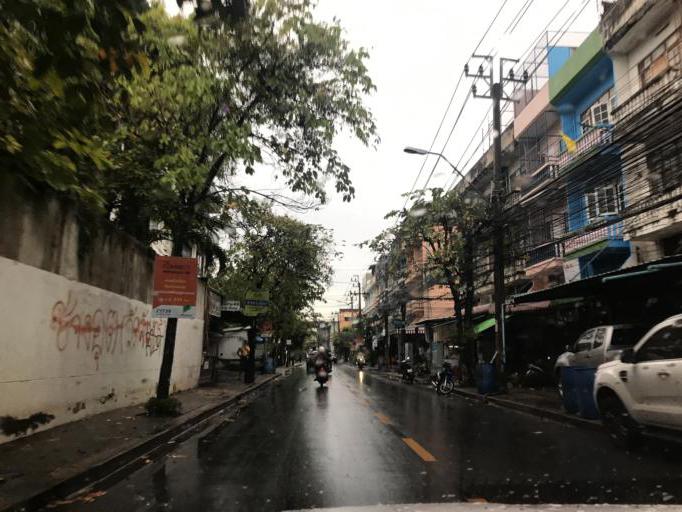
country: TH
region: Bangkok
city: Phasi Charoen
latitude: 13.7280
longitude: 100.4346
